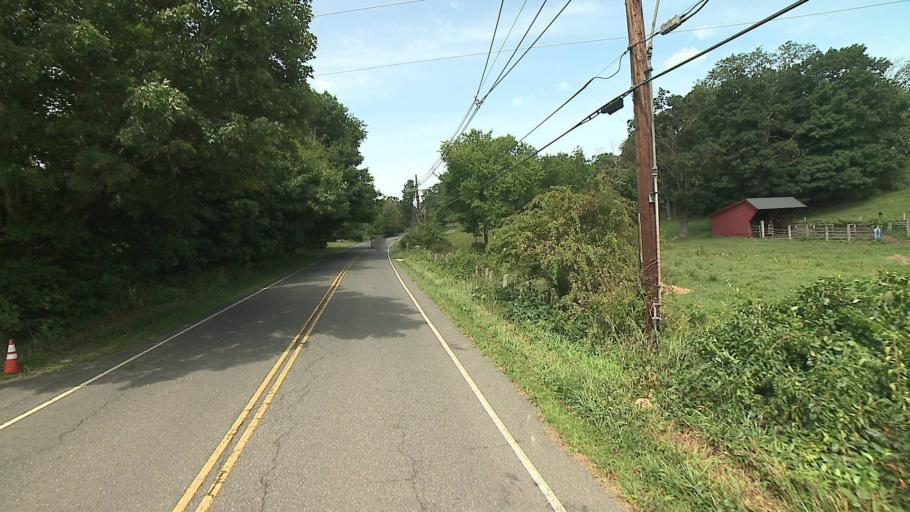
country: US
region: Connecticut
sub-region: Litchfield County
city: Bethlehem Village
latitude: 41.6015
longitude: -73.2408
